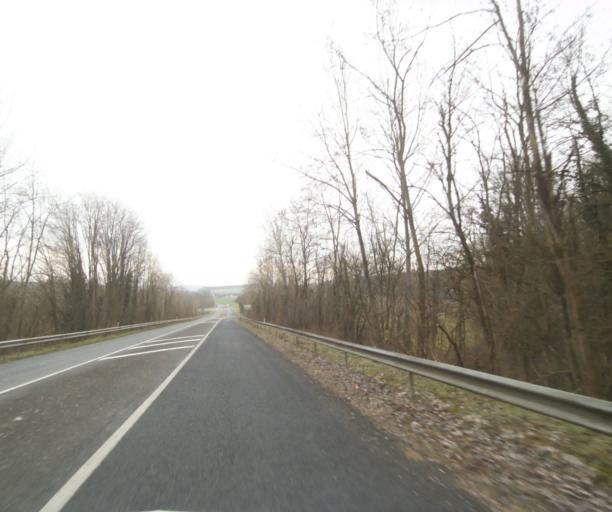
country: FR
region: Champagne-Ardenne
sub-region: Departement de la Haute-Marne
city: Bienville
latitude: 48.5696
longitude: 5.0372
